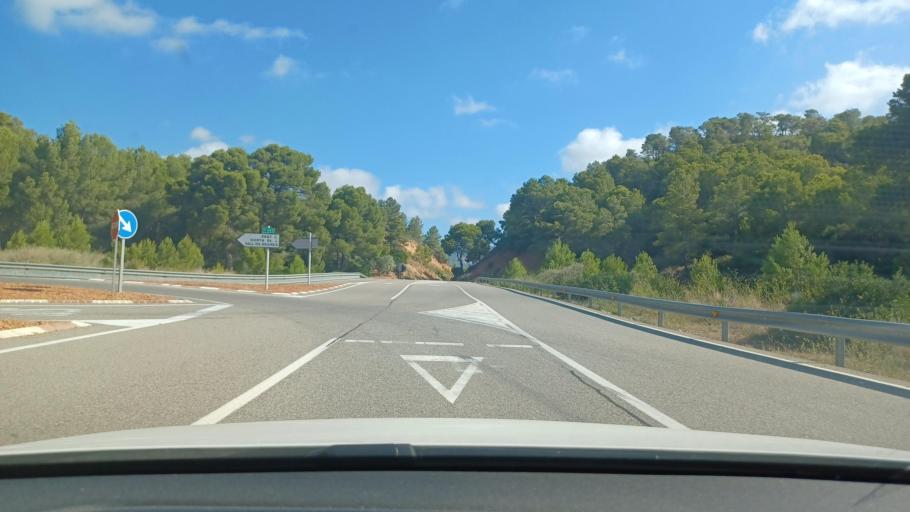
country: ES
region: Catalonia
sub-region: Provincia de Tarragona
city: Bot
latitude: 40.9734
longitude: 0.4458
